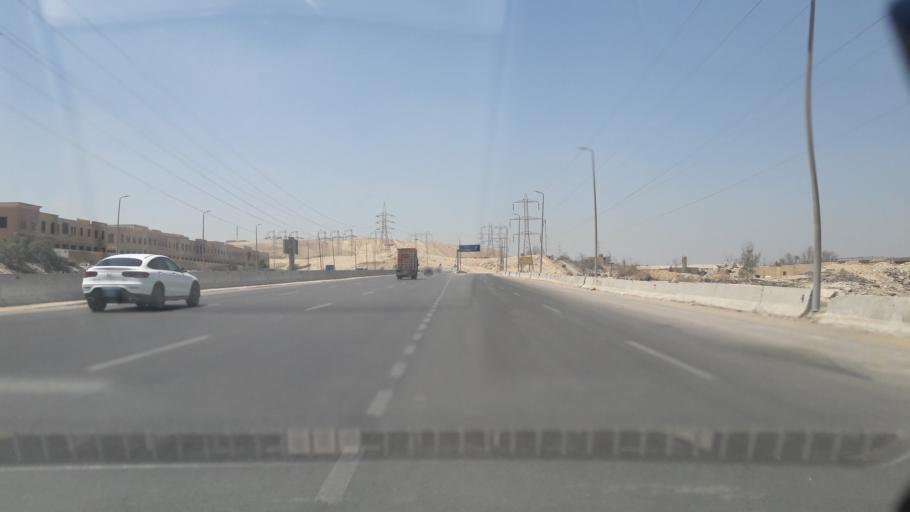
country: EG
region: Al Jizah
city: Awsim
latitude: 30.0206
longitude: 31.0819
